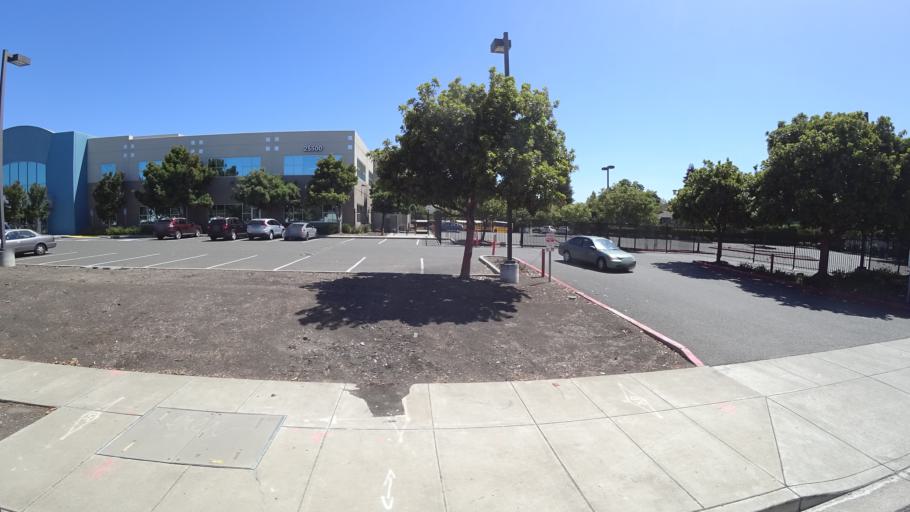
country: US
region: California
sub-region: Alameda County
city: Cherryland
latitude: 37.6362
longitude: -122.1145
